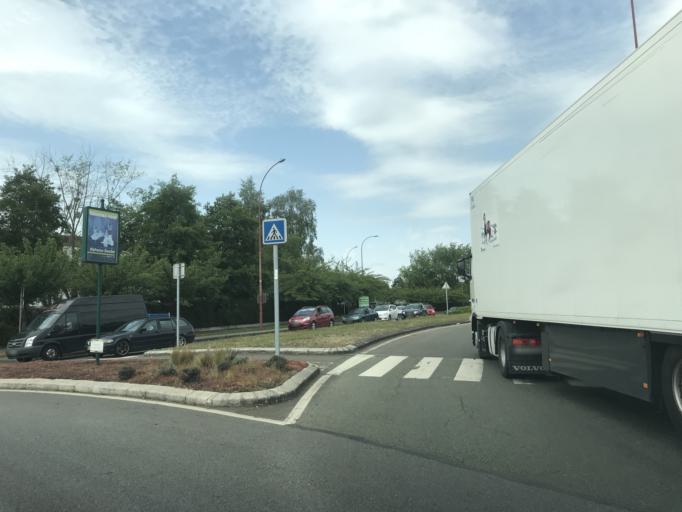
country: FR
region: Ile-de-France
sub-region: Departement des Yvelines
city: Maurepas
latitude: 48.7569
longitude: 1.9305
